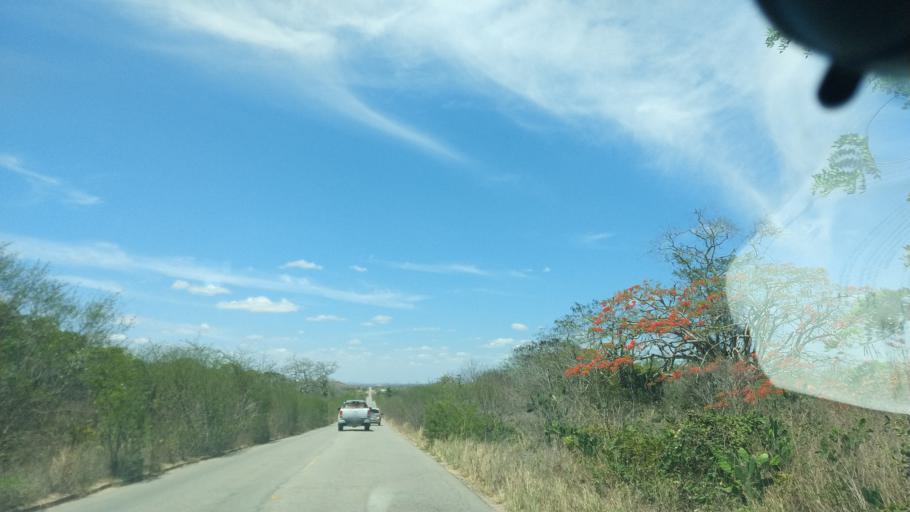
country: BR
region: Rio Grande do Norte
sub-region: Sao Paulo Do Potengi
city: Sao Paulo do Potengi
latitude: -5.9275
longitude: -35.5723
